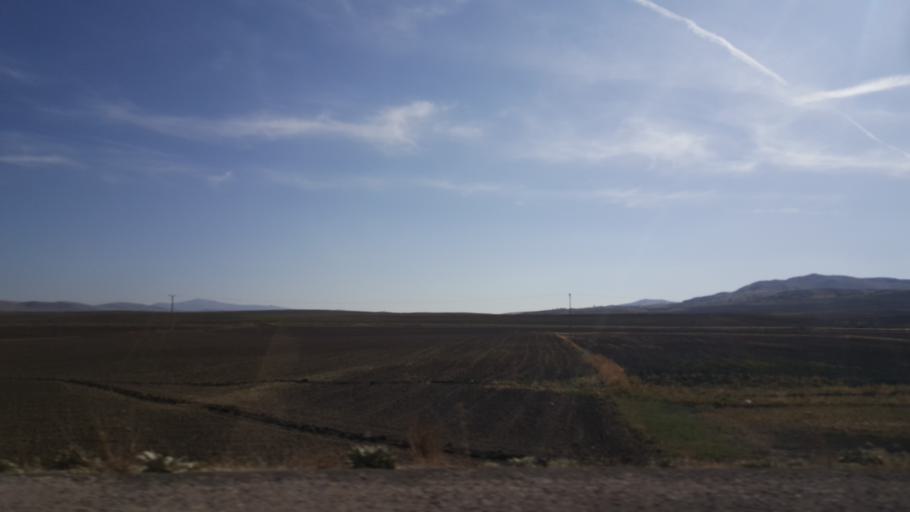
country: TR
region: Ankara
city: Yenice
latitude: 39.3755
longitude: 32.7394
